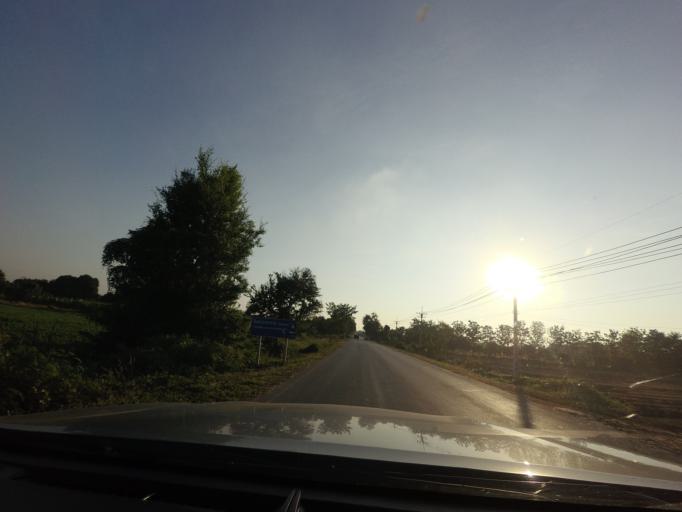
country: TH
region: Sukhothai
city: Sawankhalok
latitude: 17.3255
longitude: 99.8205
